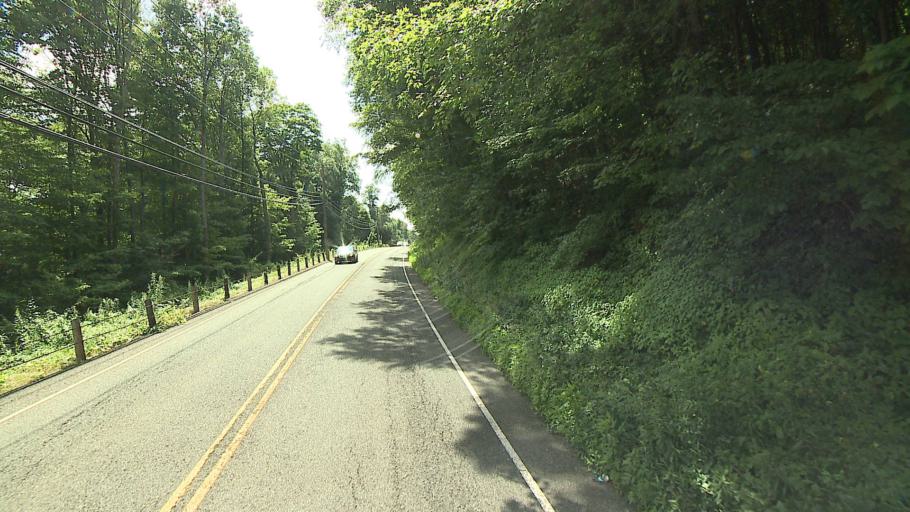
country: US
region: Connecticut
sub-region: Fairfield County
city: Sherman
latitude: 41.5593
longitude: -73.4905
